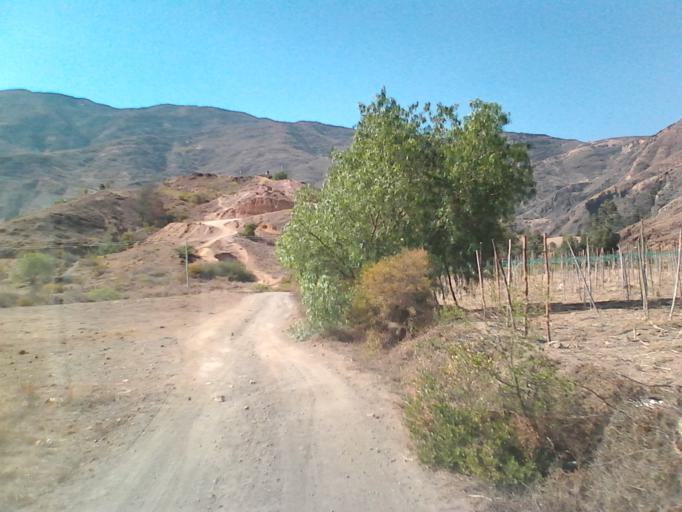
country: CO
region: Boyaca
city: Sachica
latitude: 5.5644
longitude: -73.5475
